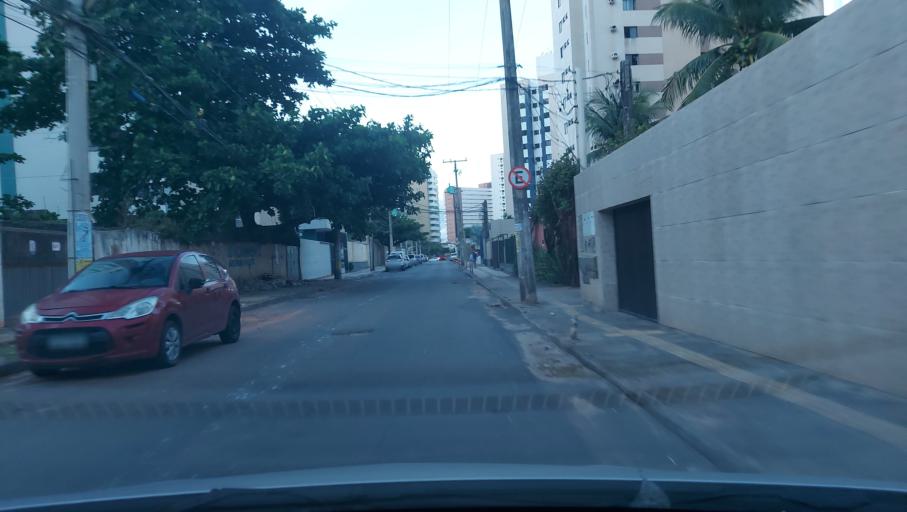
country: BR
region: Bahia
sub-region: Salvador
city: Salvador
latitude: -12.9889
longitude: -38.4391
